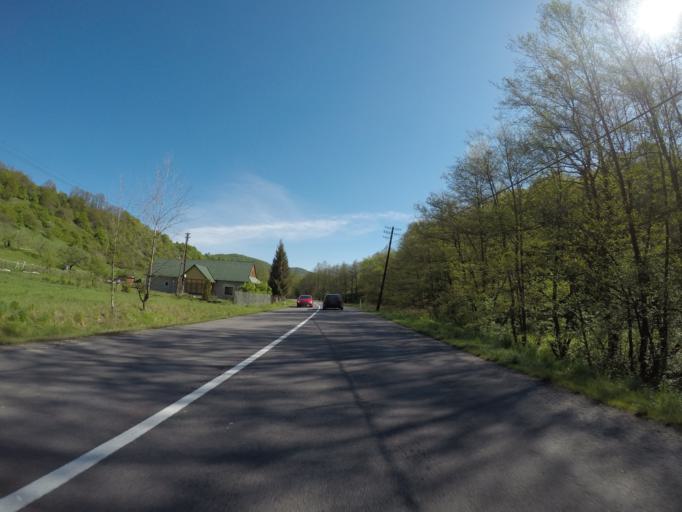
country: SK
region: Banskobystricky
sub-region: Okres Banska Bystrica
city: Banska Stiavnica
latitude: 48.4898
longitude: 18.9488
